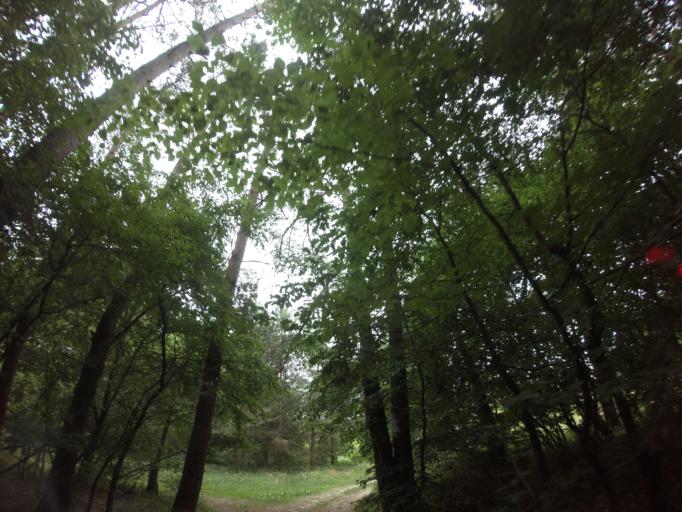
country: PL
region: West Pomeranian Voivodeship
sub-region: Powiat choszczenski
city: Bierzwnik
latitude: 53.0322
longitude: 15.6569
